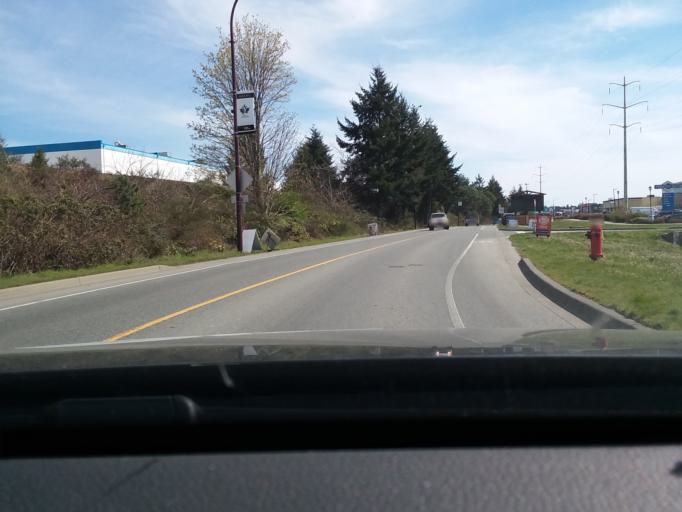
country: CA
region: British Columbia
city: Langford
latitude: 48.4435
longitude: -123.5191
